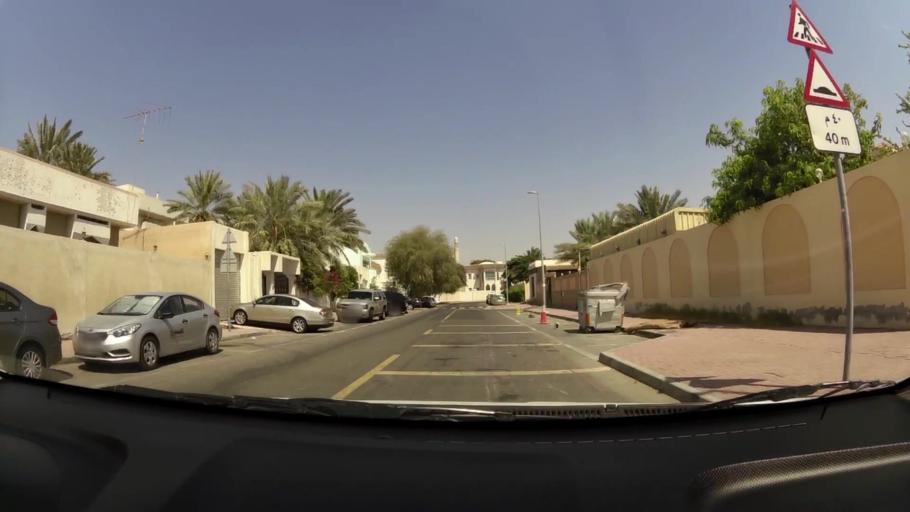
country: AE
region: Ash Shariqah
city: Sharjah
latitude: 25.2724
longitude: 55.3686
